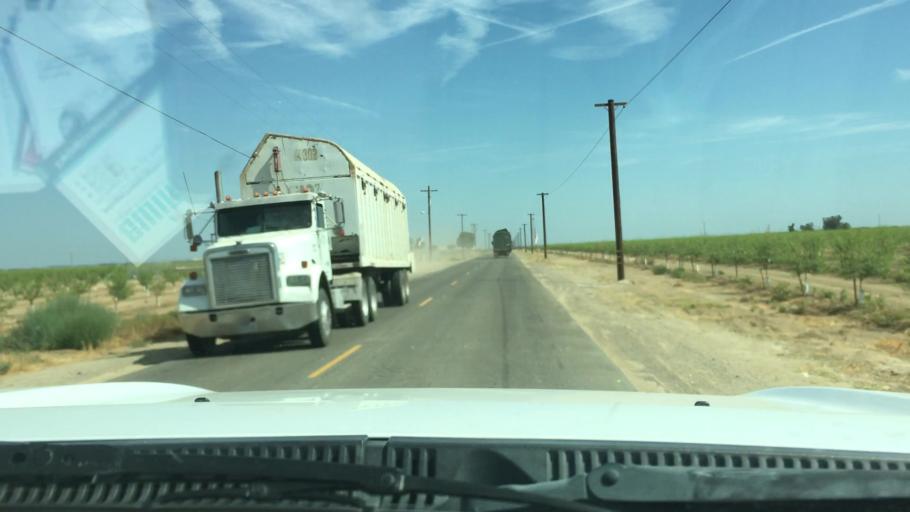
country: US
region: California
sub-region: Kern County
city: Shafter
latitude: 35.4590
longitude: -119.3681
